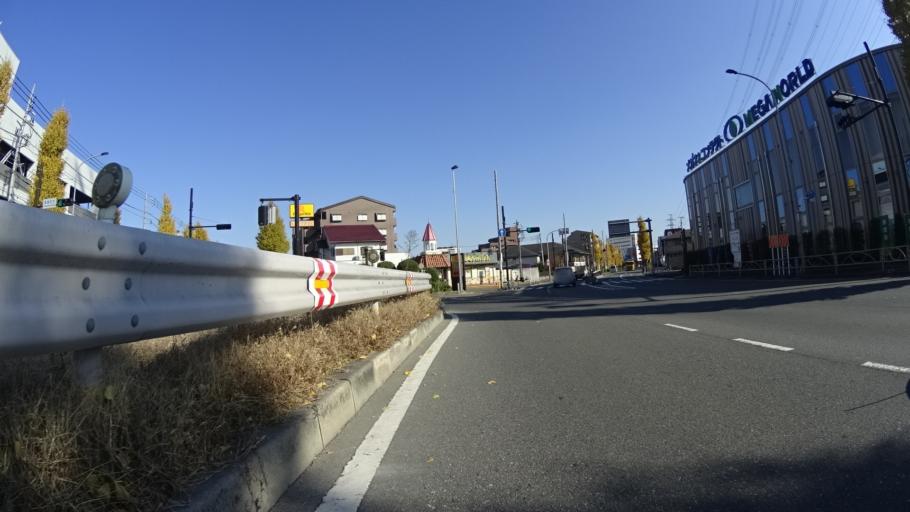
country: JP
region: Tokyo
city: Hino
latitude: 35.6661
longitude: 139.3643
